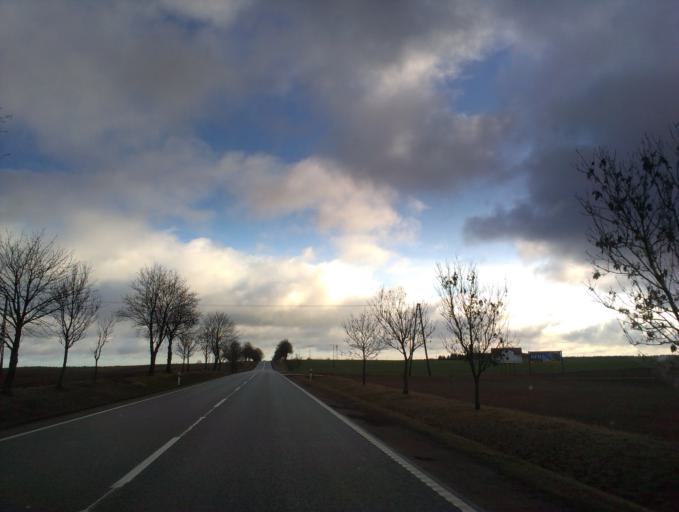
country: PL
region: Pomeranian Voivodeship
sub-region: Powiat czluchowski
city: Czluchow
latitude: 53.6336
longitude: 17.2716
